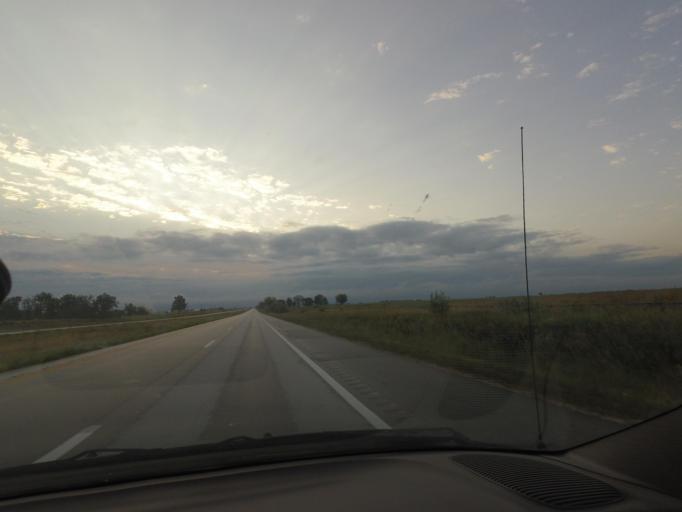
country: US
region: Missouri
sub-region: Shelby County
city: Shelbina
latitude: 39.7119
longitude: -92.1179
